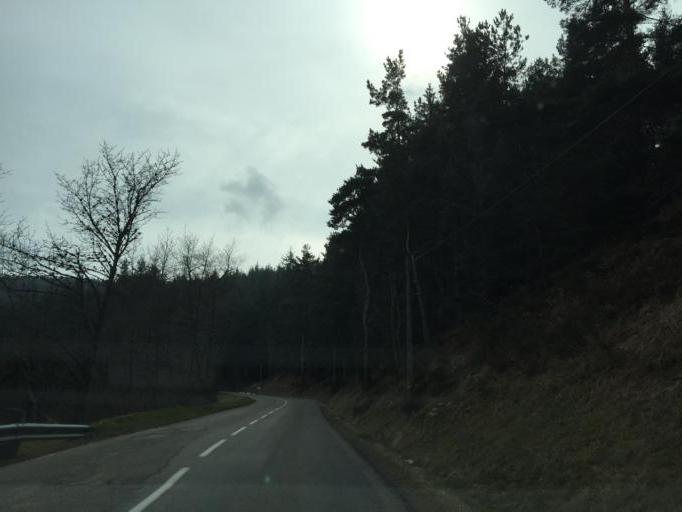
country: FR
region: Rhone-Alpes
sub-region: Departement de la Loire
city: Saint-Chamond
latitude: 45.3994
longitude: 4.5332
